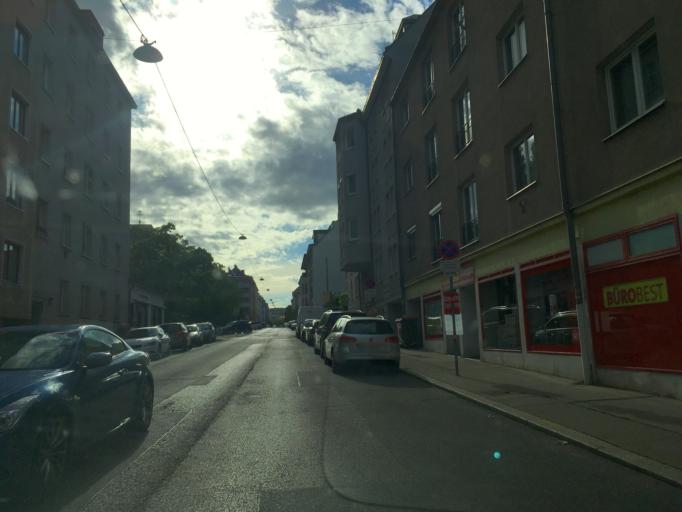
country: AT
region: Vienna
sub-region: Wien Stadt
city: Vienna
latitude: 48.2432
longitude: 16.3388
